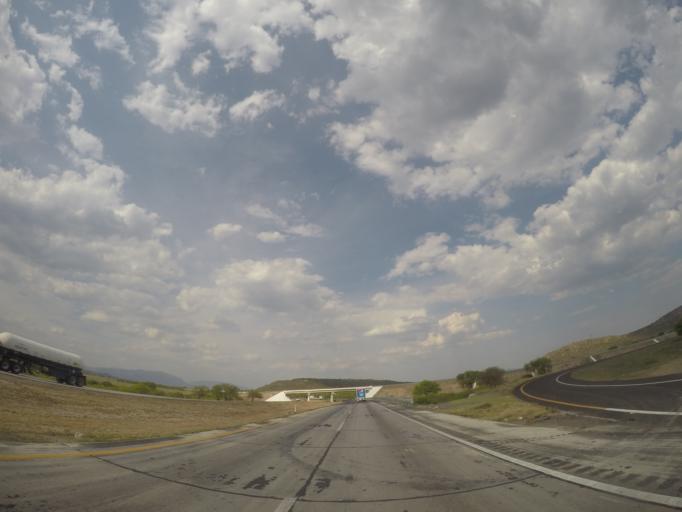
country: MX
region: San Luis Potosi
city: Cerritos
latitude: 22.5007
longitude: -100.6677
